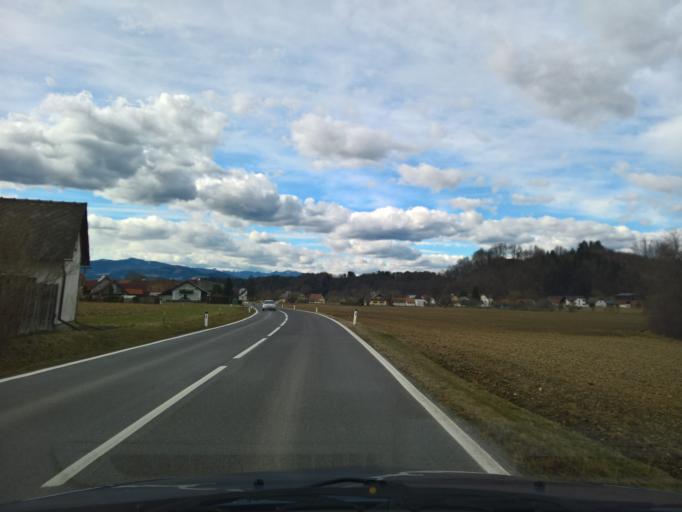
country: AT
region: Styria
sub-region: Politischer Bezirk Leibnitz
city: Oberhaag
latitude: 46.6951
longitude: 15.3141
